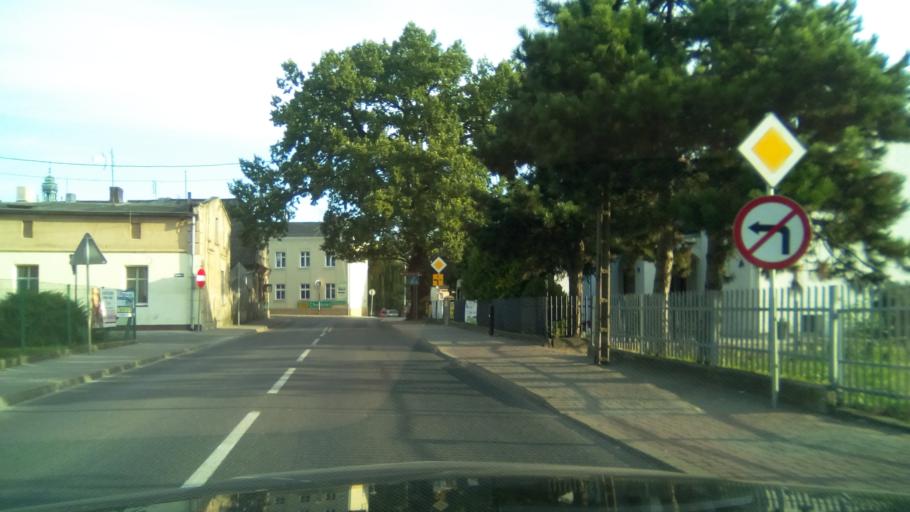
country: PL
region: Greater Poland Voivodeship
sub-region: Powiat gnieznienski
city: Klecko
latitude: 52.6311
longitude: 17.4307
